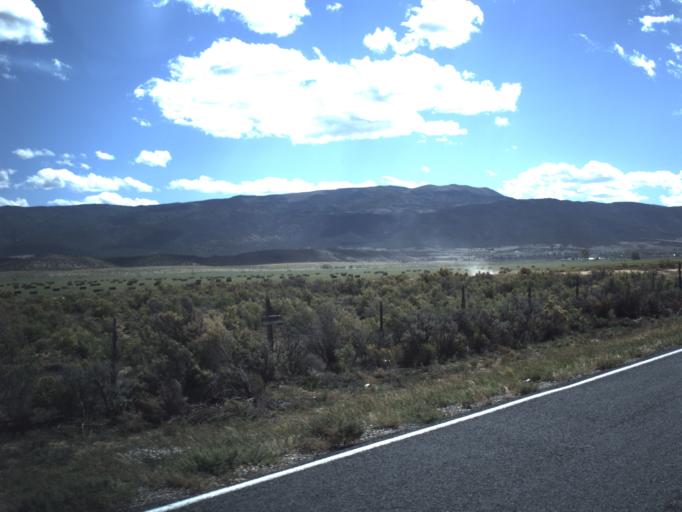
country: US
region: Utah
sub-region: Iron County
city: Enoch
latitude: 37.8155
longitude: -113.0505
